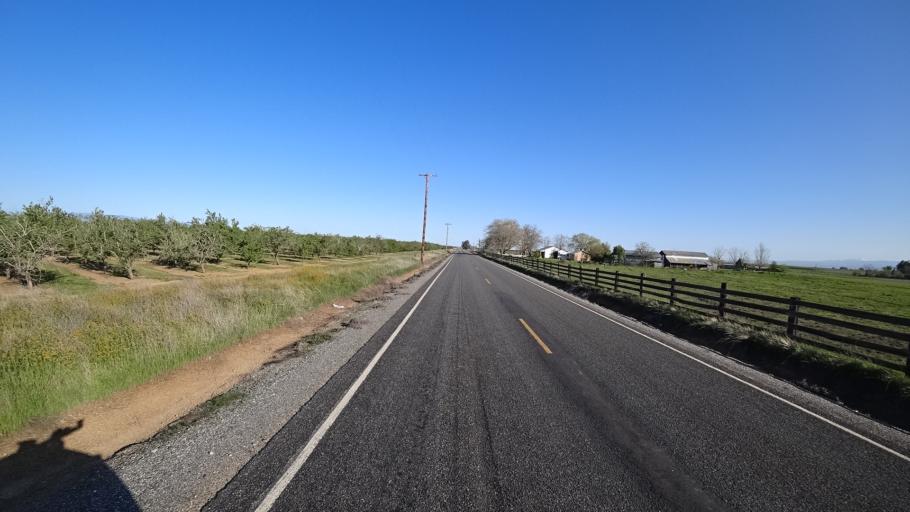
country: US
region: California
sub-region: Glenn County
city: Orland
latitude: 39.7937
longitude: -122.1229
